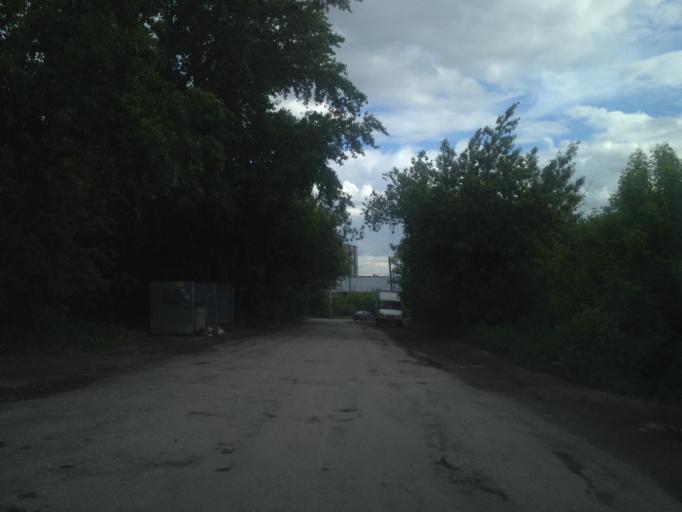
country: RU
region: Sverdlovsk
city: Yekaterinburg
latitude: 56.8612
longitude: 60.5822
